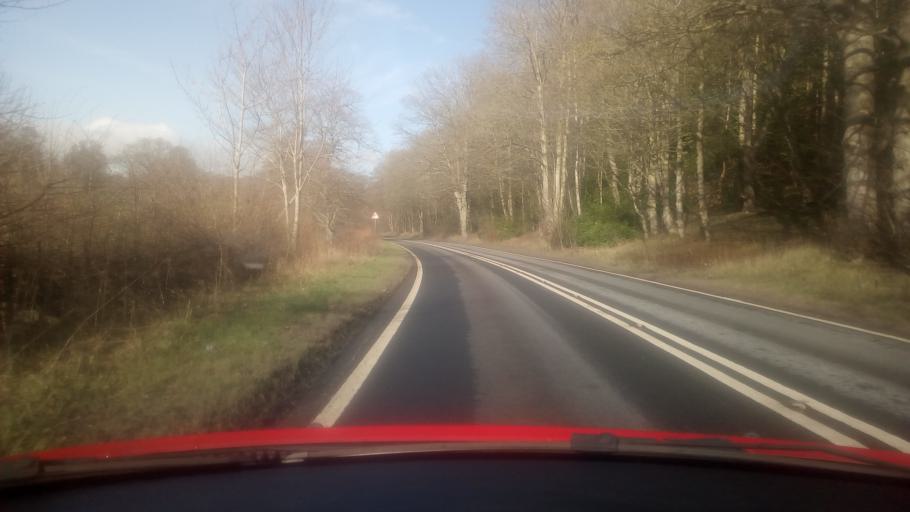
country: GB
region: Scotland
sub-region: The Scottish Borders
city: Jedburgh
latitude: 55.5201
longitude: -2.5829
